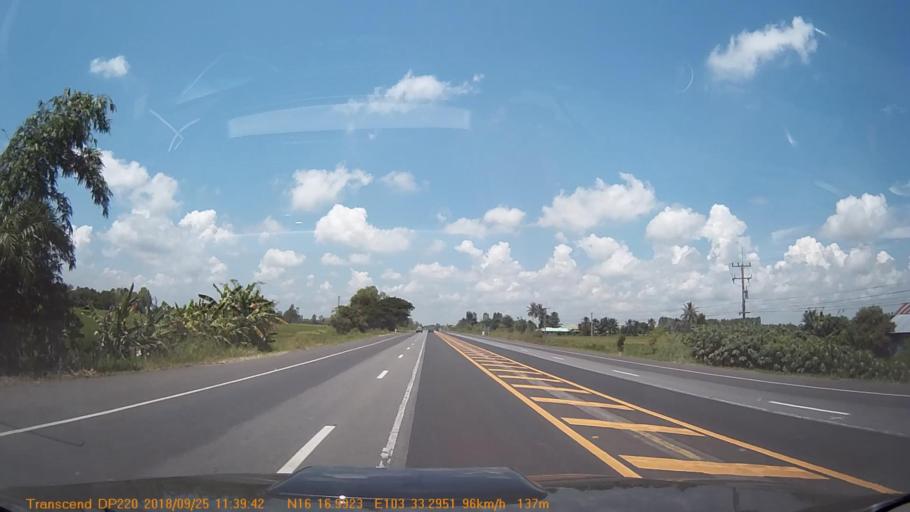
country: TH
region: Kalasin
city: Kamalasai
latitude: 16.2830
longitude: 103.5551
